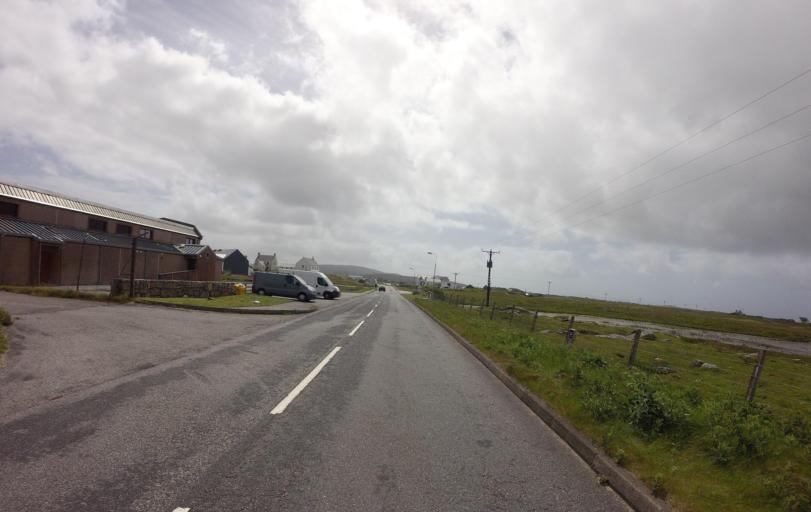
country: GB
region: Scotland
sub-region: Eilean Siar
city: Isle of South Uist
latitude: 57.1699
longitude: -7.3746
